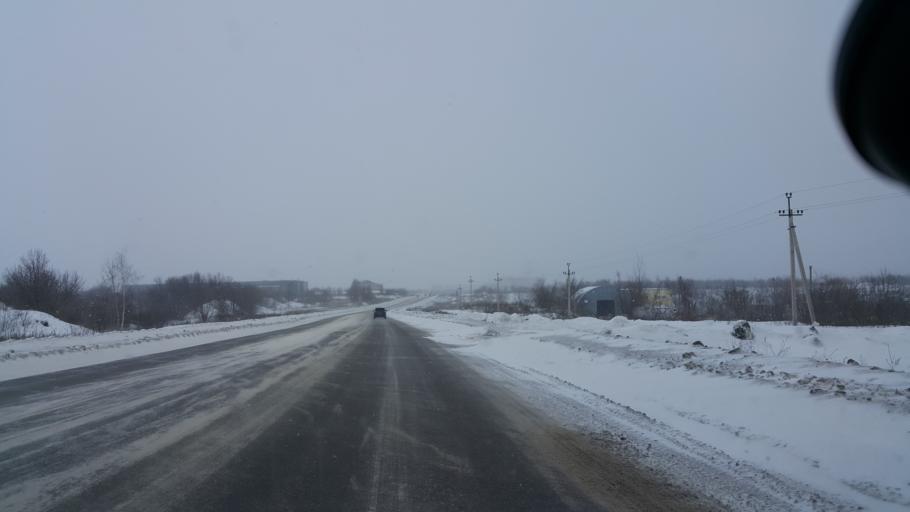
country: RU
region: Tambov
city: Tambov
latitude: 52.7413
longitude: 41.3792
